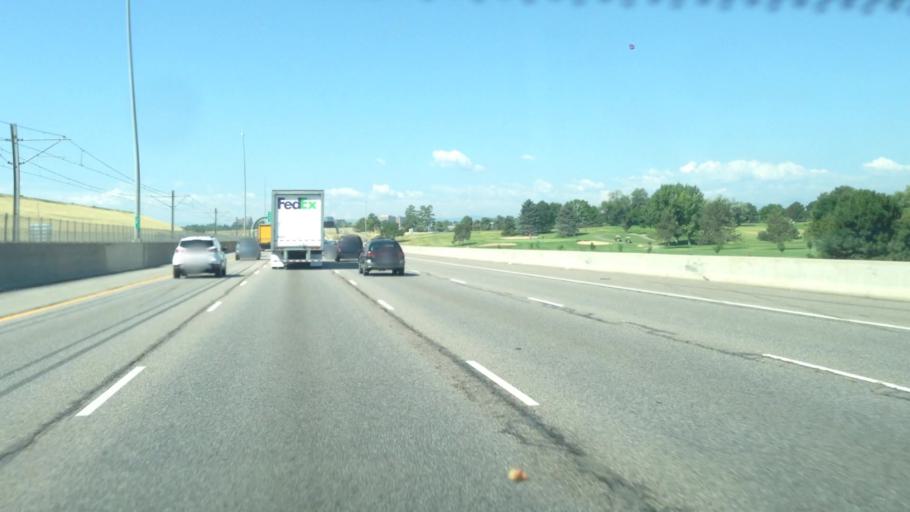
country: US
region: Colorado
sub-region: Arapahoe County
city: Centennial
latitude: 39.6497
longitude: -104.8629
